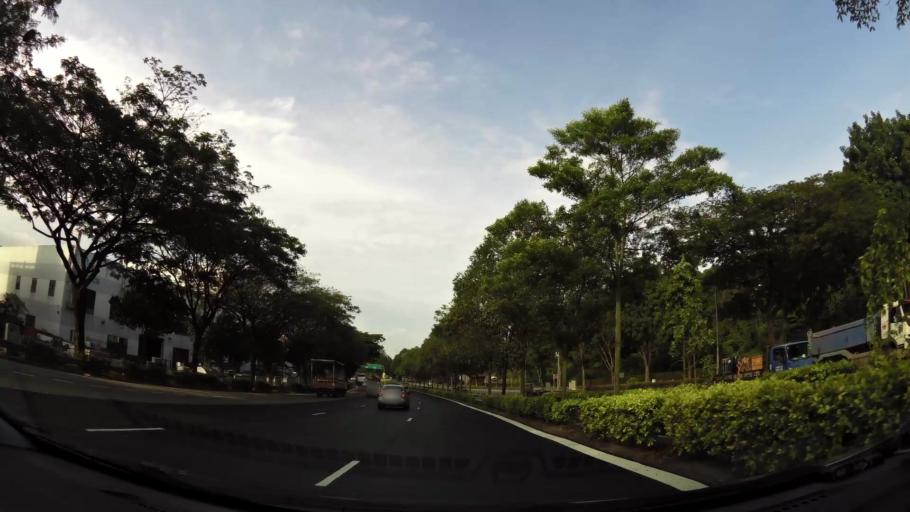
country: MY
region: Johor
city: Johor Bahru
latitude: 1.3300
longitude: 103.6719
